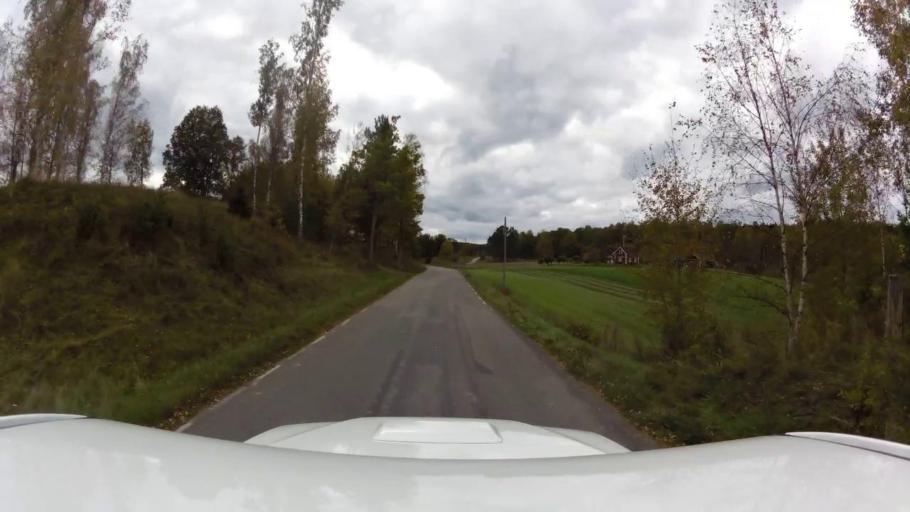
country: SE
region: OEstergoetland
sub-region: Kinda Kommun
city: Rimforsa
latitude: 58.1960
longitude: 15.5686
